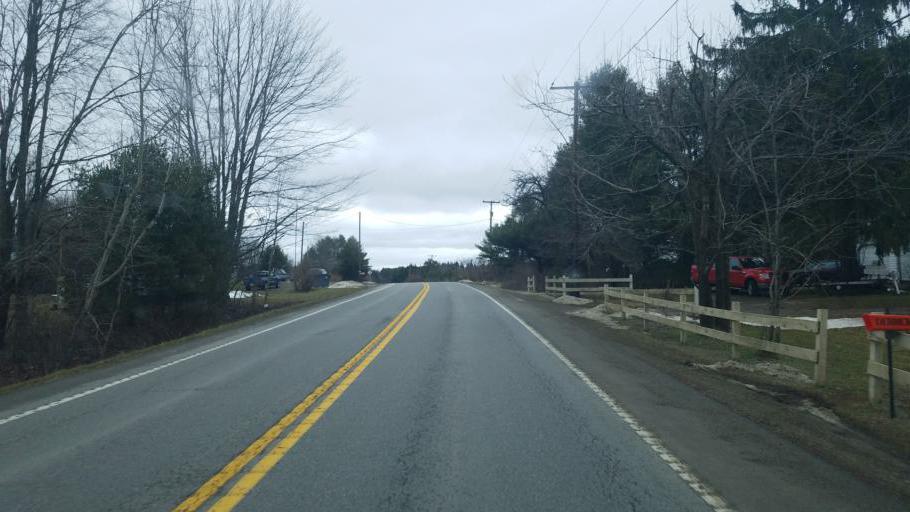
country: US
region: Pennsylvania
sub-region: Forest County
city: Marienville
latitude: 41.4322
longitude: -79.1881
